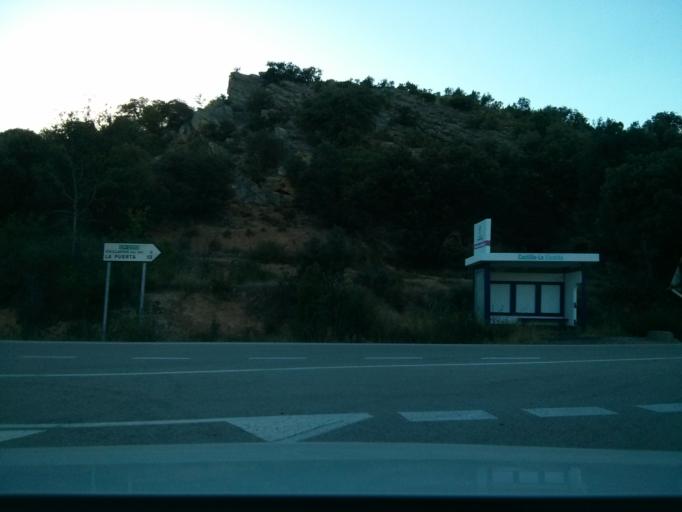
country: ES
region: Castille-La Mancha
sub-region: Provincia de Guadalajara
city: Chillaron del Rey
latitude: 40.5860
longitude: -2.7035
